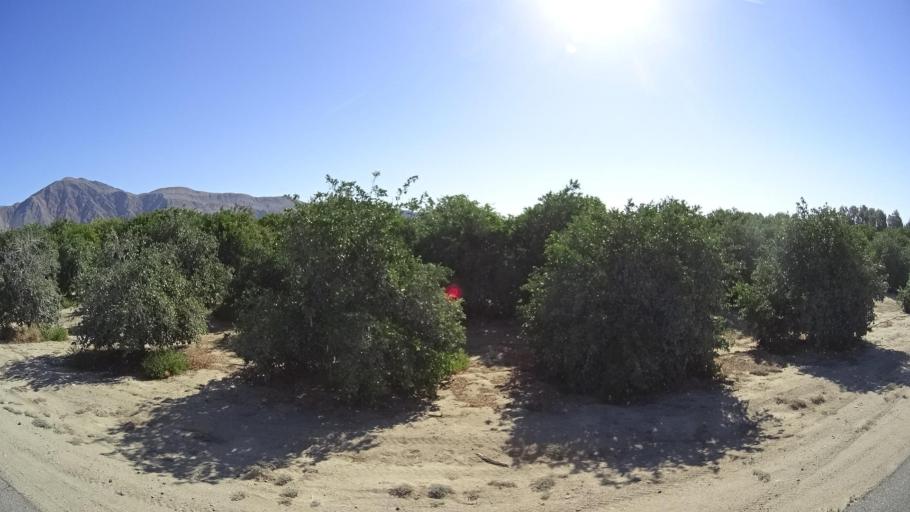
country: US
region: California
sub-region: San Diego County
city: Borrego Springs
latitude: 33.3019
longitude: -116.3668
